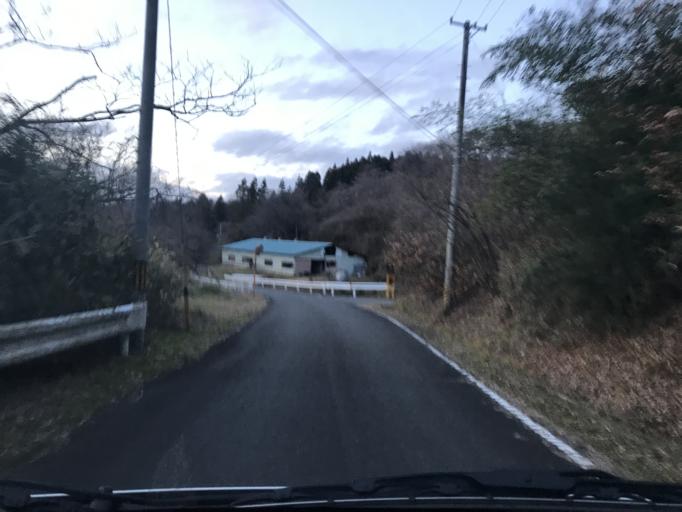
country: JP
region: Iwate
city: Ichinoseki
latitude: 38.8314
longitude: 141.0891
